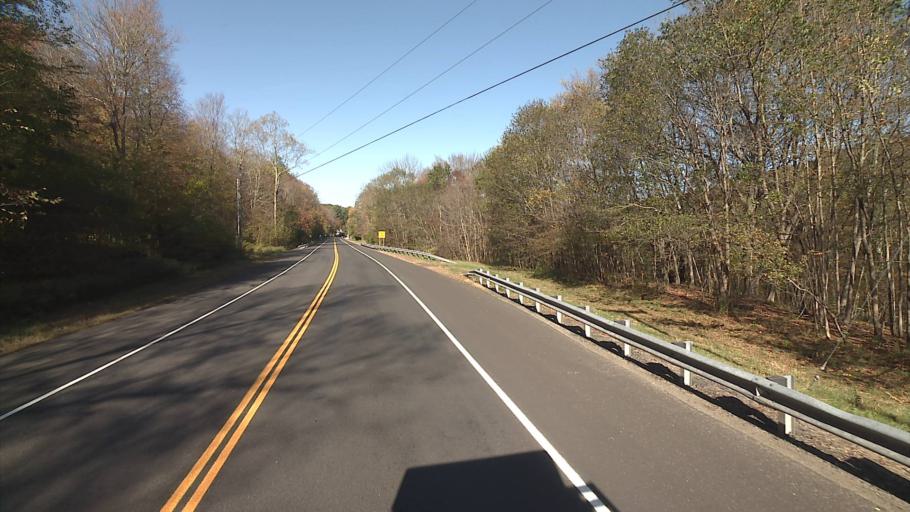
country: US
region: Connecticut
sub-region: Tolland County
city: Coventry Lake
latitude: 41.7708
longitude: -72.4090
